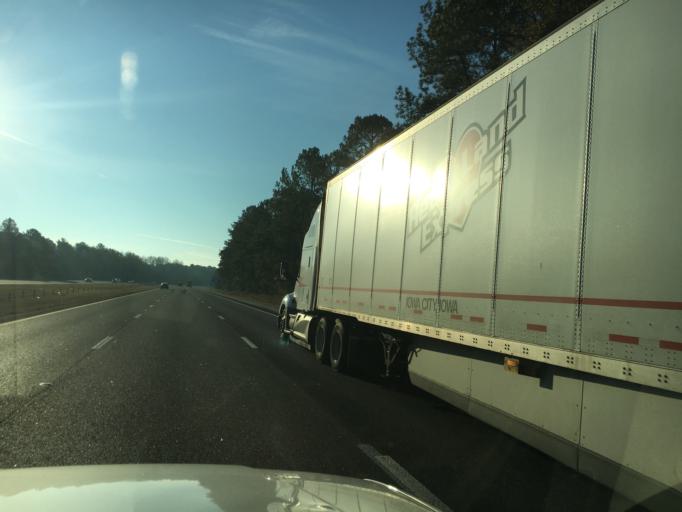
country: US
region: South Carolina
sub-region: Lexington County
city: Pineridge
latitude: 33.8898
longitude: -81.0407
